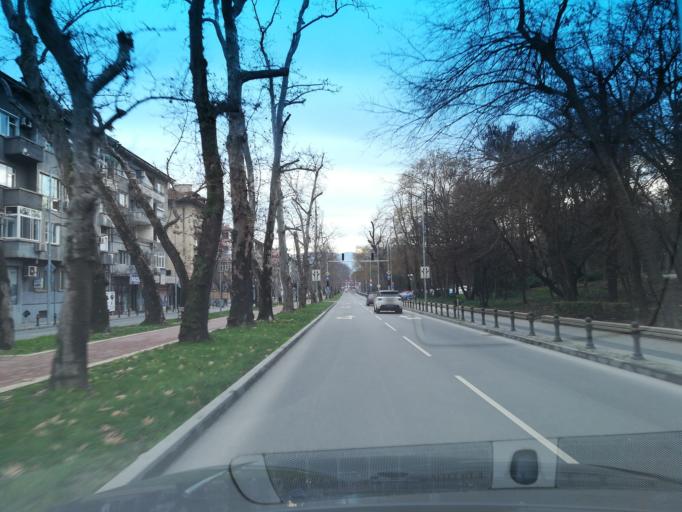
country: BG
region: Plovdiv
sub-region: Obshtina Plovdiv
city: Plovdiv
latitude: 42.1452
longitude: 24.7411
